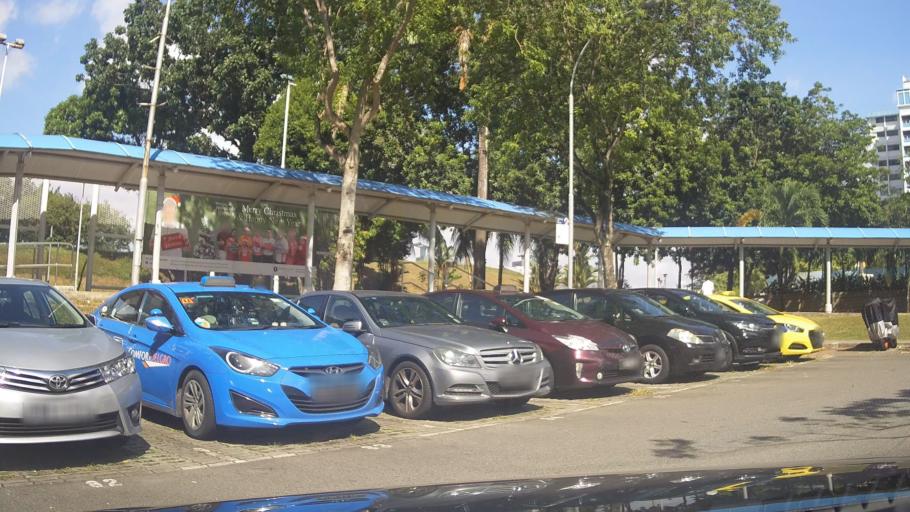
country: MY
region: Johor
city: Johor Bahru
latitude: 1.4421
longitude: 103.7722
